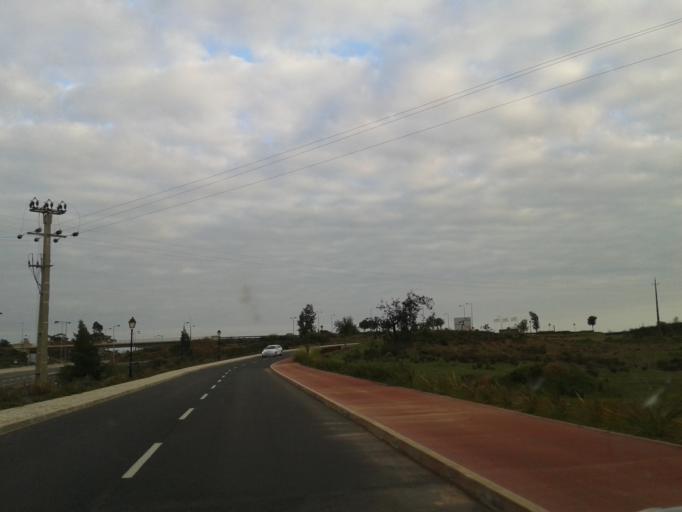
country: PT
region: Faro
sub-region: Castro Marim
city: Castro Marim
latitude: 37.2423
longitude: -7.4567
